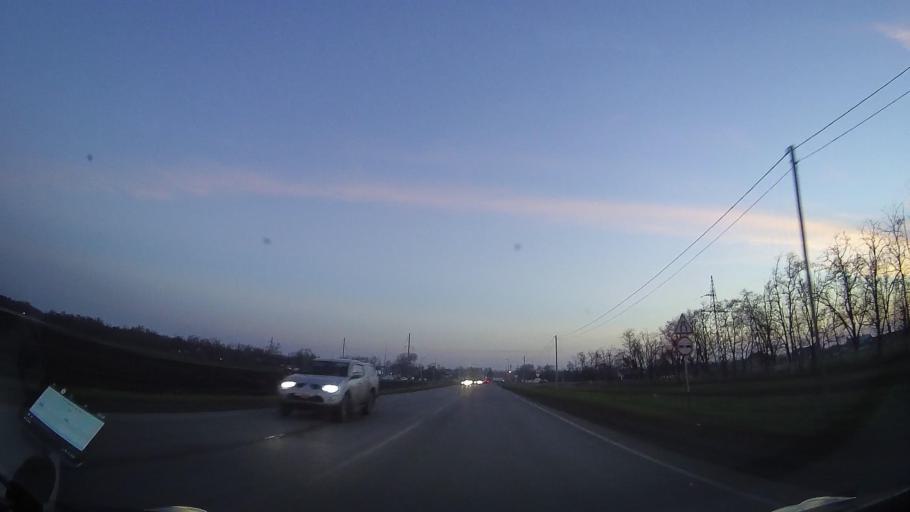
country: RU
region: Rostov
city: Zernograd
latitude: 46.8132
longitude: 40.2994
